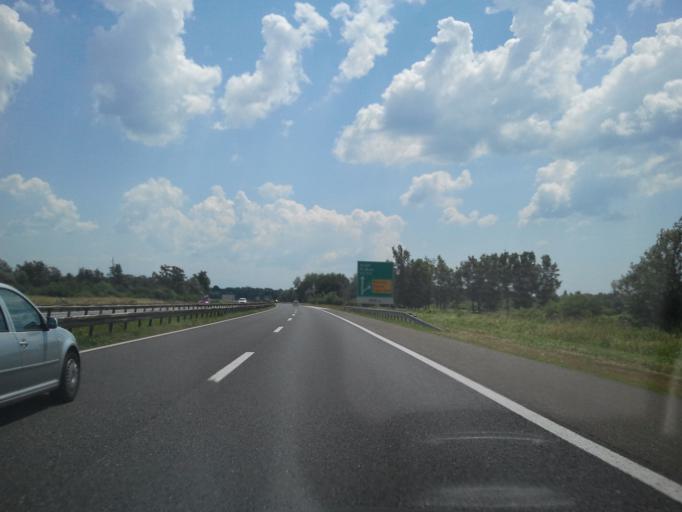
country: HR
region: Zagrebacka
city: Lupoglav
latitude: 45.6921
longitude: 16.3714
